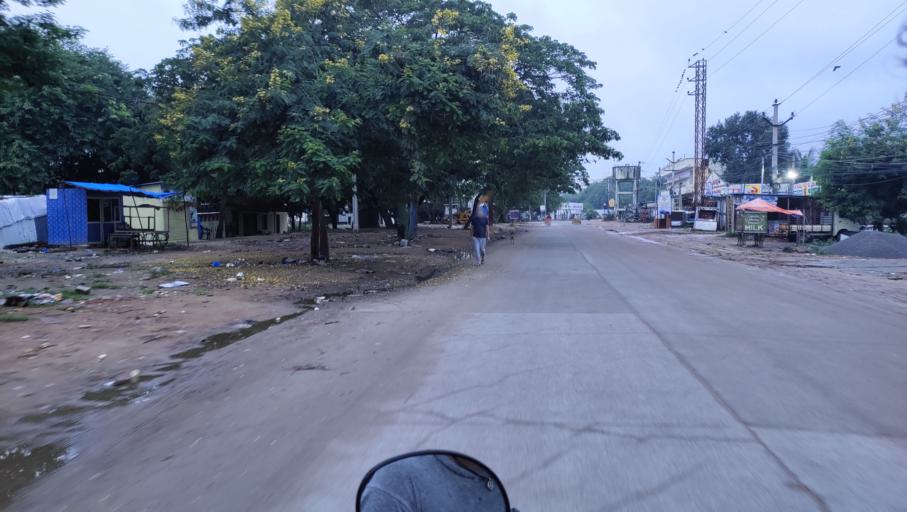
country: IN
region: Telangana
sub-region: Hyderabad
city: Hyderabad
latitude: 17.4010
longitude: 78.3722
